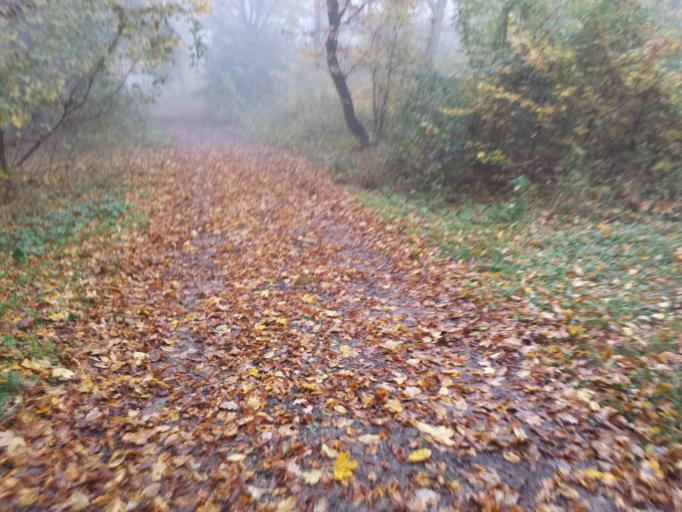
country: RO
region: Cluj
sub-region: Comuna Baciu
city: Baciu
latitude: 46.7727
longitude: 23.5455
